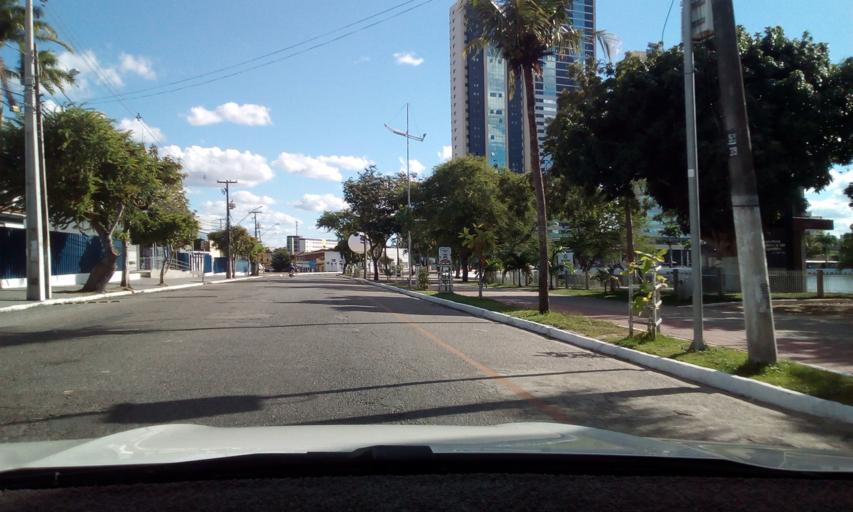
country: BR
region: Paraiba
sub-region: Campina Grande
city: Campina Grande
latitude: -7.2275
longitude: -35.8818
